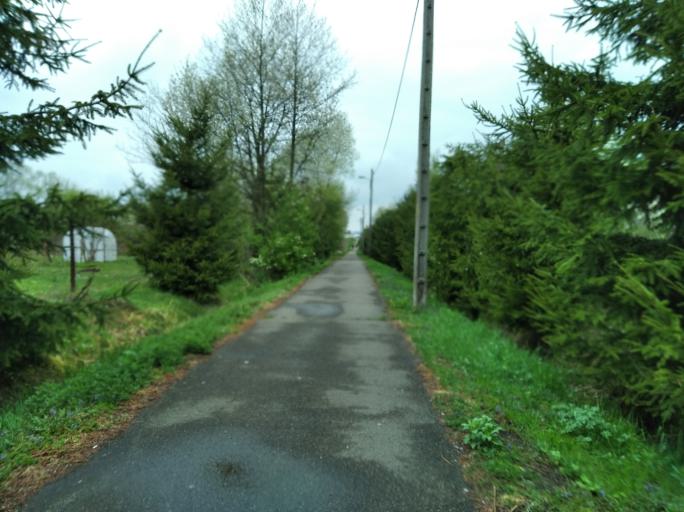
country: PL
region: Subcarpathian Voivodeship
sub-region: Powiat brzozowski
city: Brzozow
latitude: 49.7040
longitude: 22.0161
